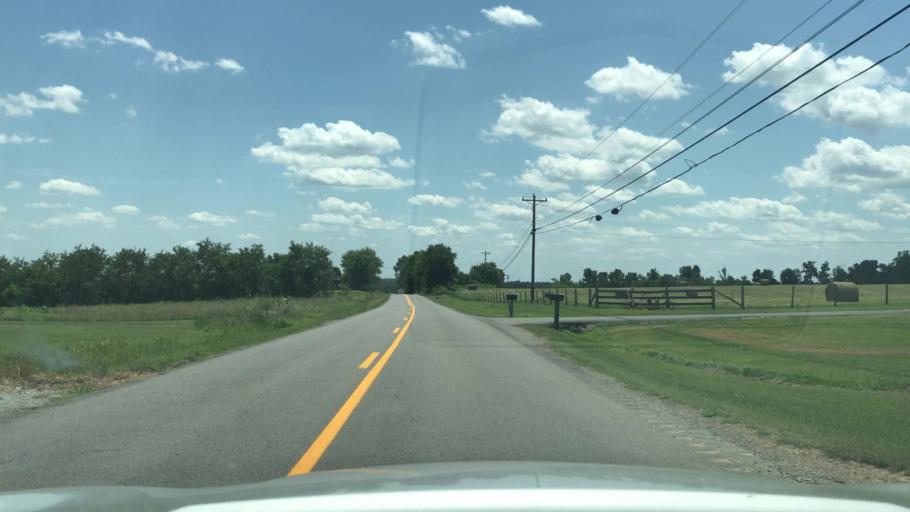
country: US
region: Kentucky
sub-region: Christian County
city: Hopkinsville
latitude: 36.9216
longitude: -87.4369
